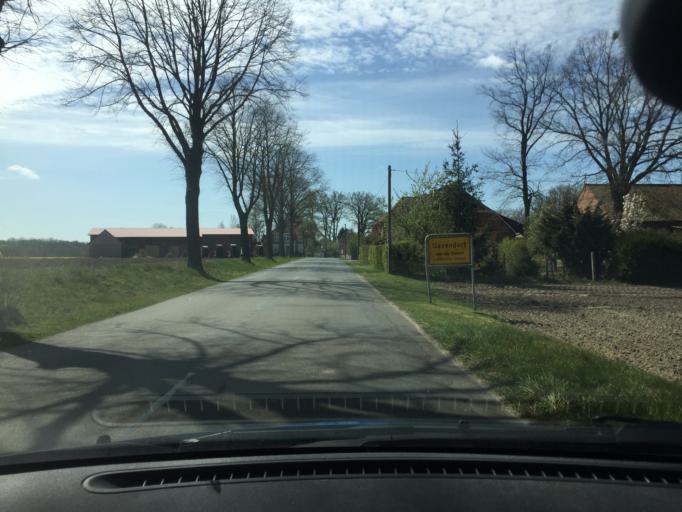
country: DE
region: Lower Saxony
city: Suhlendorf
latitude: 52.9260
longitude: 10.7120
